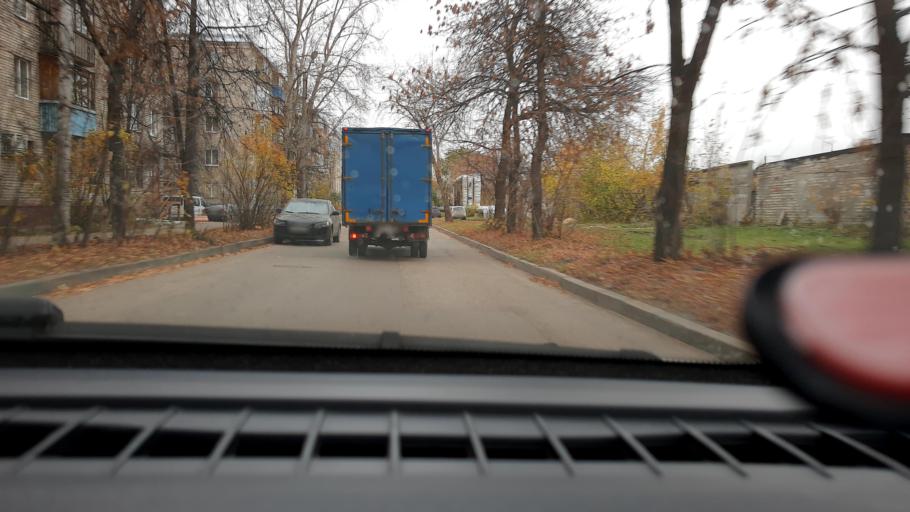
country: RU
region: Nizjnij Novgorod
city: Gorbatovka
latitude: 56.2527
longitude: 43.8700
